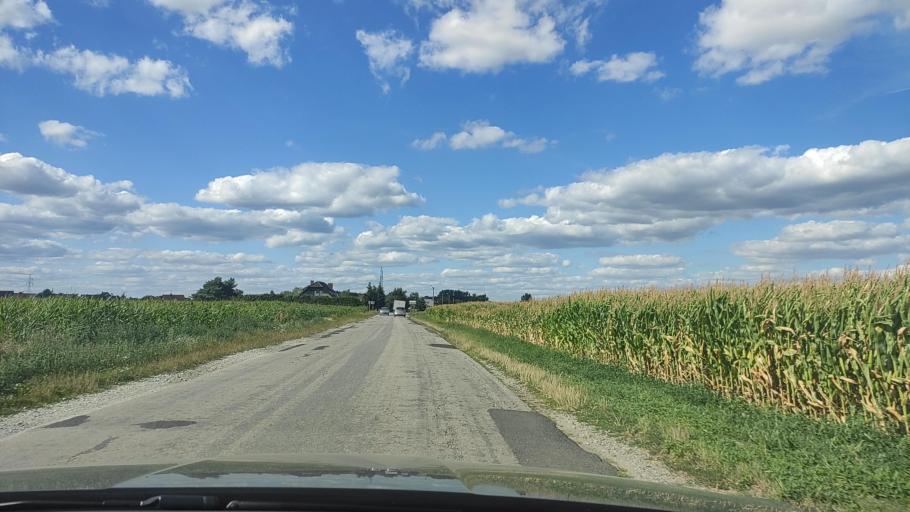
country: PL
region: Greater Poland Voivodeship
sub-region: Powiat poznanski
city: Kleszczewo
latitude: 52.3725
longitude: 17.1673
